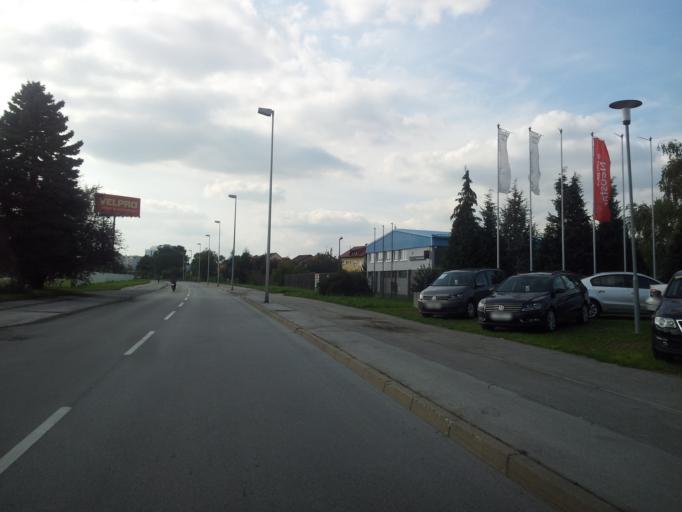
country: HR
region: Varazdinska
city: Varazdin
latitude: 46.2986
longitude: 16.3515
